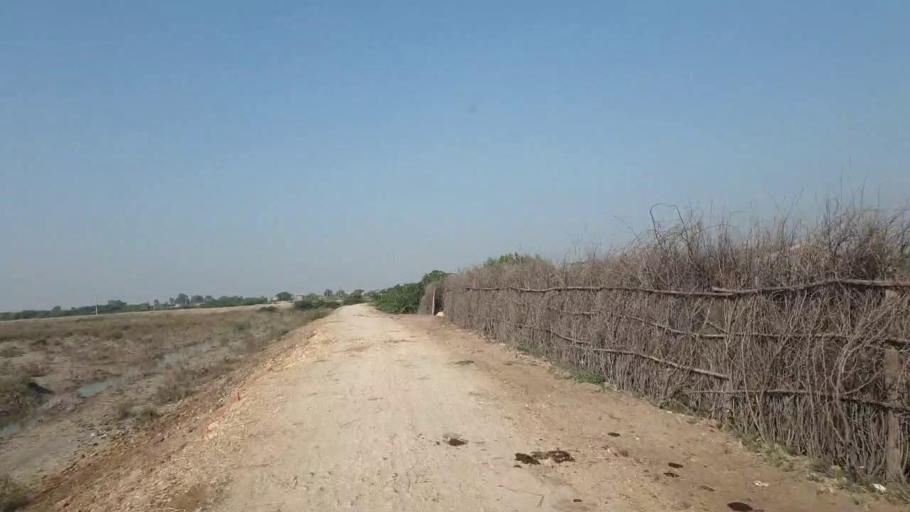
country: PK
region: Sindh
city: Badin
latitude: 24.5212
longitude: 68.7677
